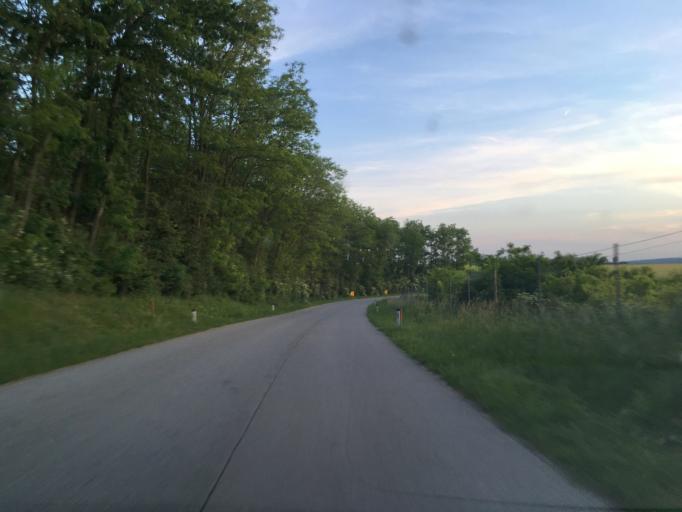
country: AT
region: Lower Austria
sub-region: Politischer Bezirk Mistelbach
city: Herrnbaumgarten
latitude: 48.7138
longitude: 16.6677
